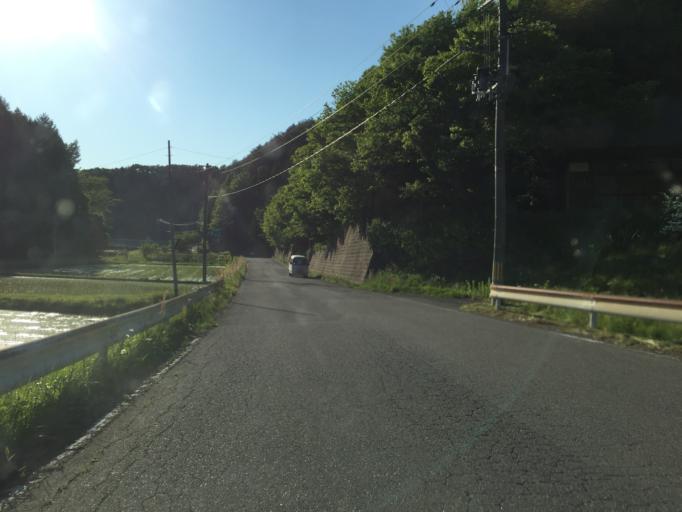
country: JP
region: Ibaraki
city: Daigo
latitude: 36.9207
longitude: 140.5317
